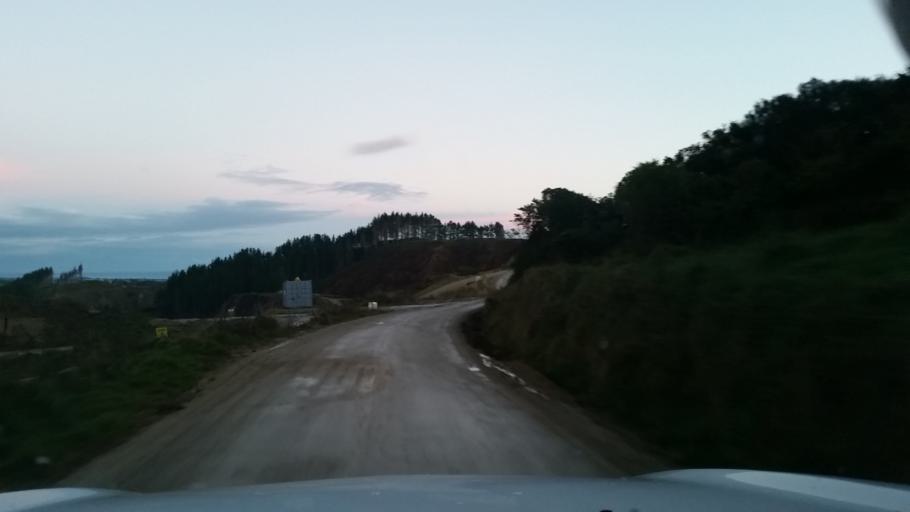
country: NZ
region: Manawatu-Wanganui
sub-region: Wanganui District
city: Wanganui
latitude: -39.7715
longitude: 174.8708
